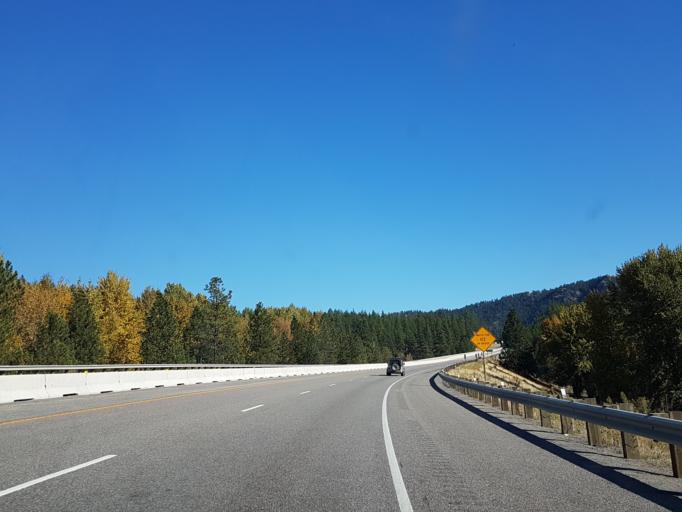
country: US
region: Montana
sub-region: Missoula County
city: Frenchtown
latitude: 47.0232
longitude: -114.3876
